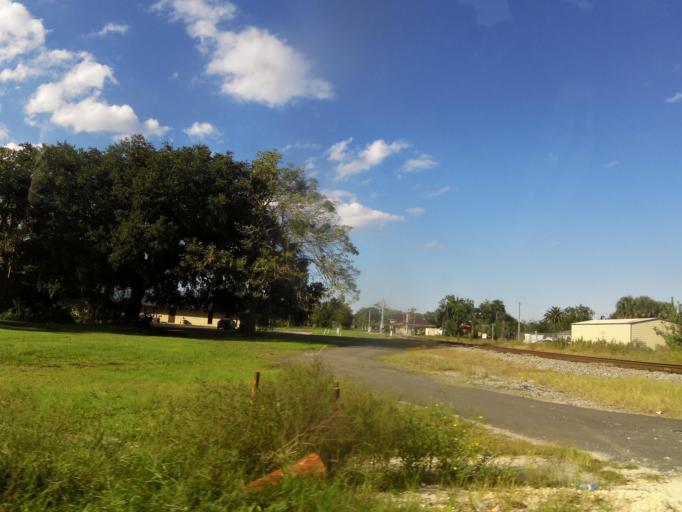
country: US
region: Florida
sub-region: Putnam County
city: Palatka
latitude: 29.6481
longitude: -81.6413
